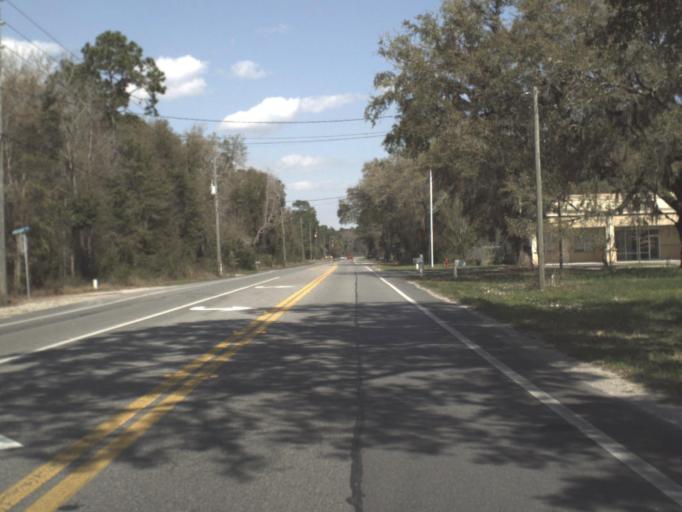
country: US
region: Florida
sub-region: Wakulla County
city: Crawfordville
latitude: 30.0730
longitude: -84.4374
